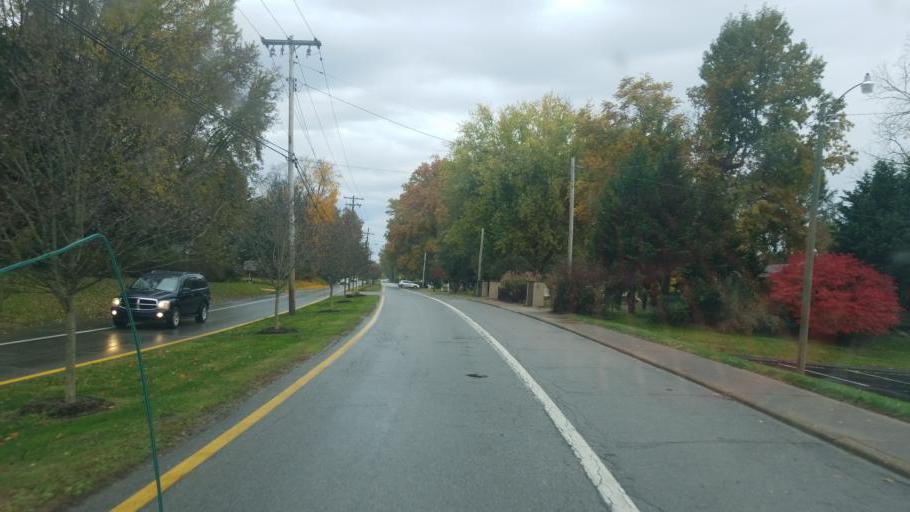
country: US
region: West Virginia
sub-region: Wood County
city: Vienna
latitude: 39.3433
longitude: -81.5383
